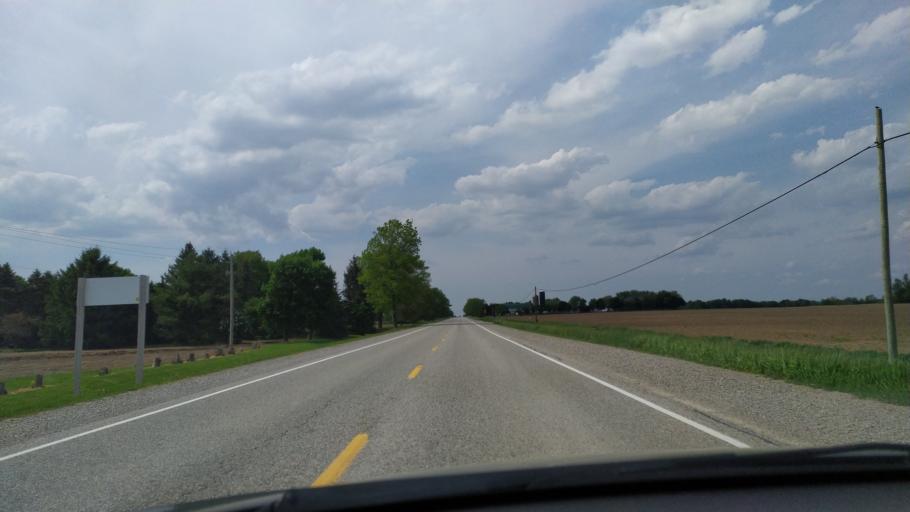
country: CA
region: Ontario
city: Dorchester
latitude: 43.1130
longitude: -81.0169
